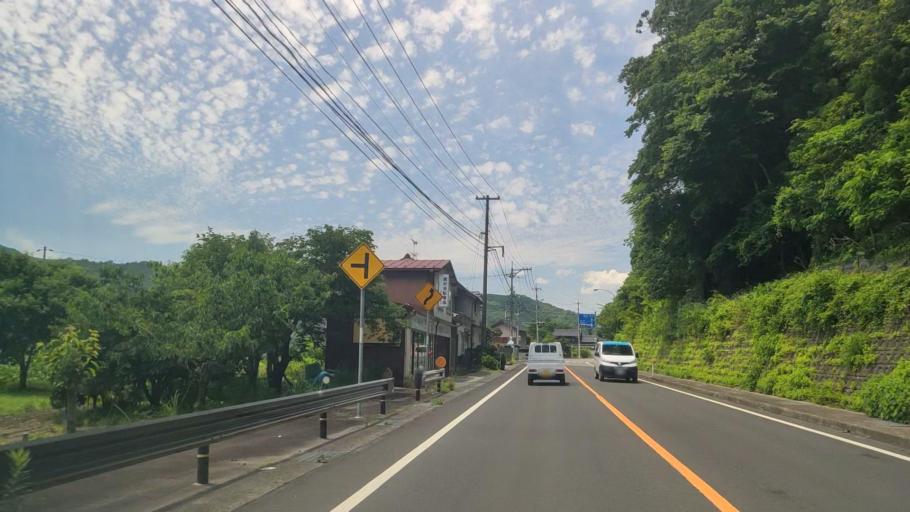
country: JP
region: Tottori
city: Tottori
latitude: 35.3663
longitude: 134.3210
